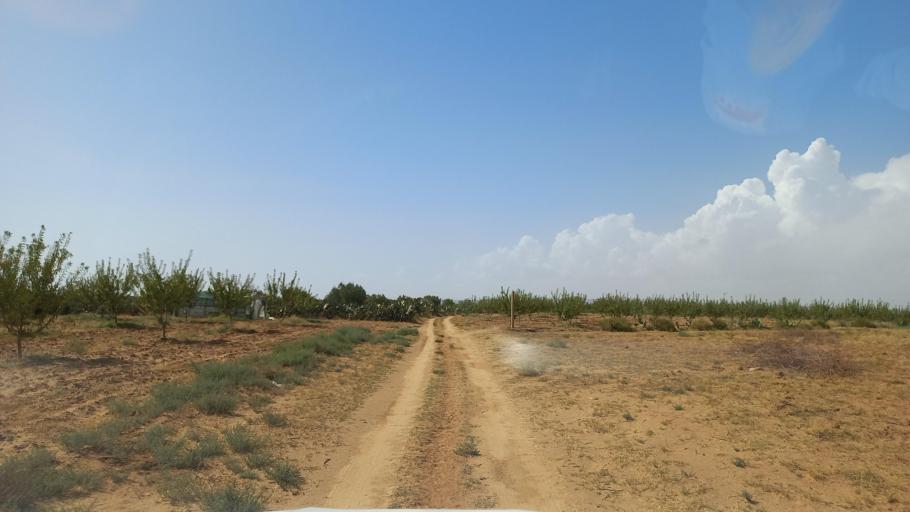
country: TN
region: Al Qasrayn
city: Kasserine
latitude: 35.2114
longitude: 9.0346
